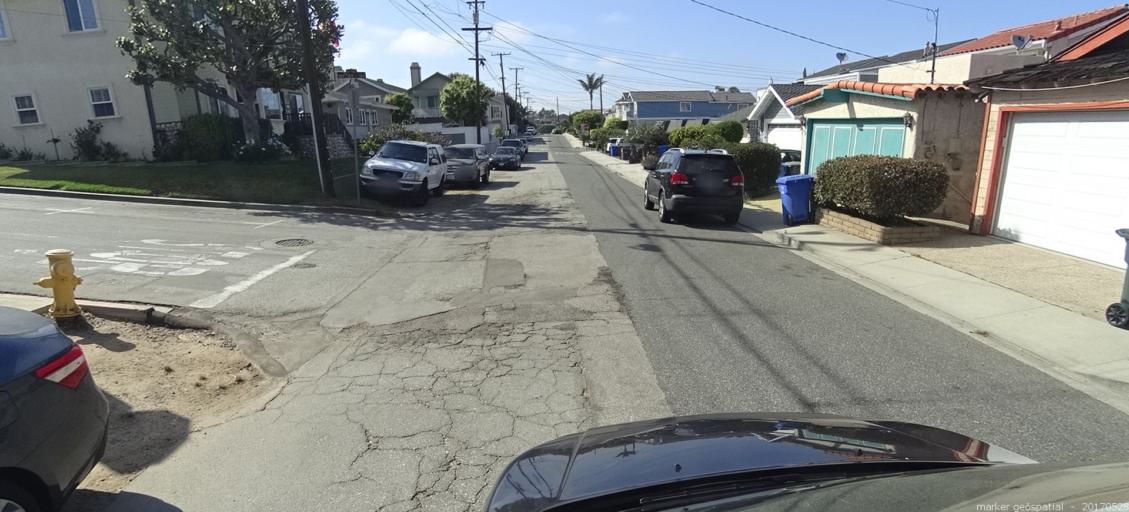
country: US
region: California
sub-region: Los Angeles County
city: Hermosa Beach
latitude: 33.8706
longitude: -118.3900
